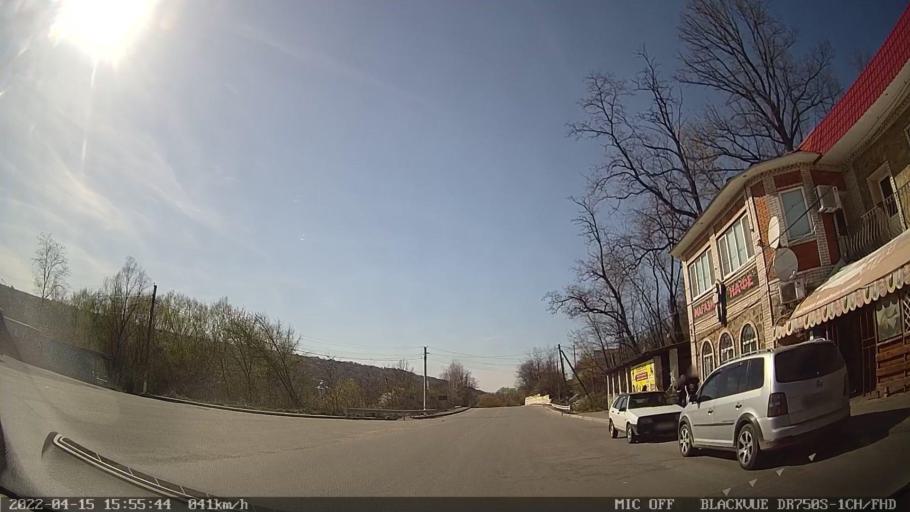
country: MD
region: Raionul Ocnita
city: Otaci
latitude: 48.4003
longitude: 27.8801
